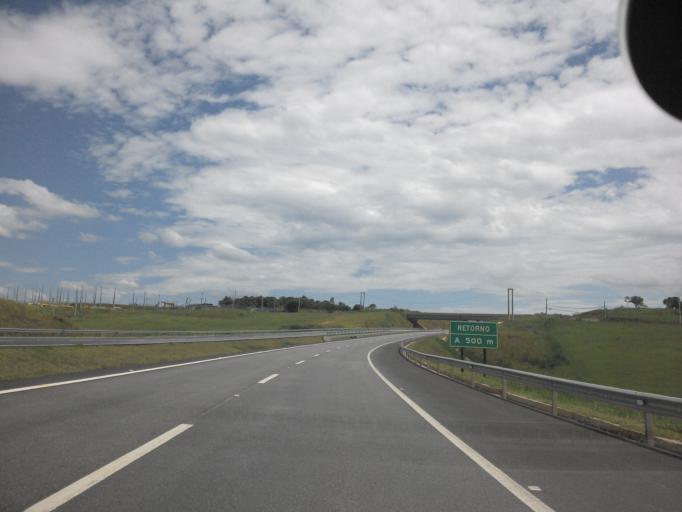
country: BR
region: Sao Paulo
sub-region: Taubate
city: Taubate
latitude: -23.0919
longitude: -45.5718
